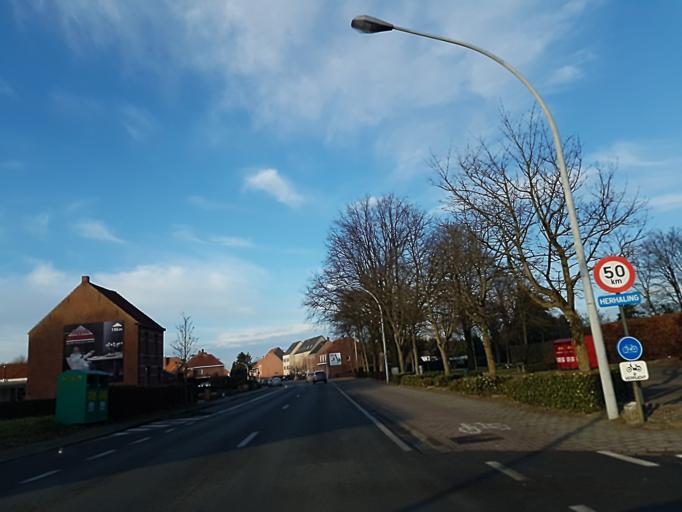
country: BE
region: Flanders
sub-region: Provincie Antwerpen
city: Ravels
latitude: 51.3715
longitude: 4.9938
